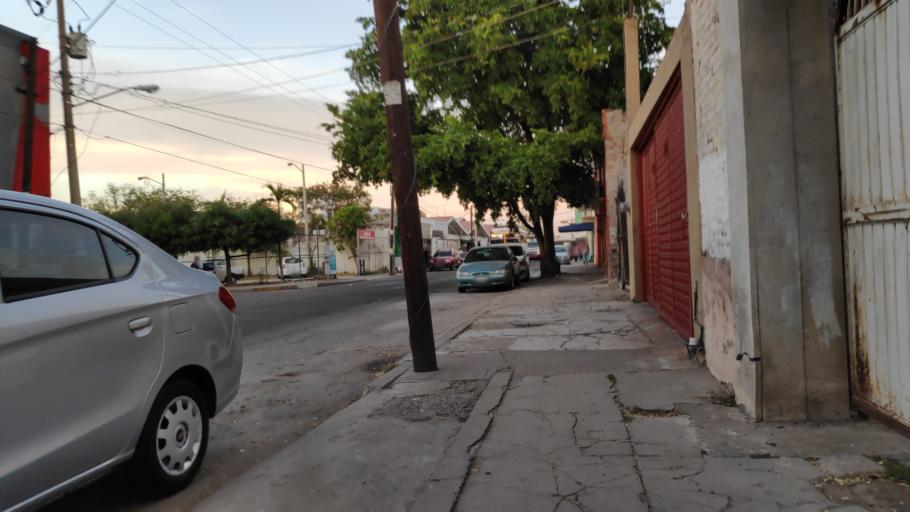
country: MX
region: Sinaloa
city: Culiacan
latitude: 24.8027
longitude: -107.3956
